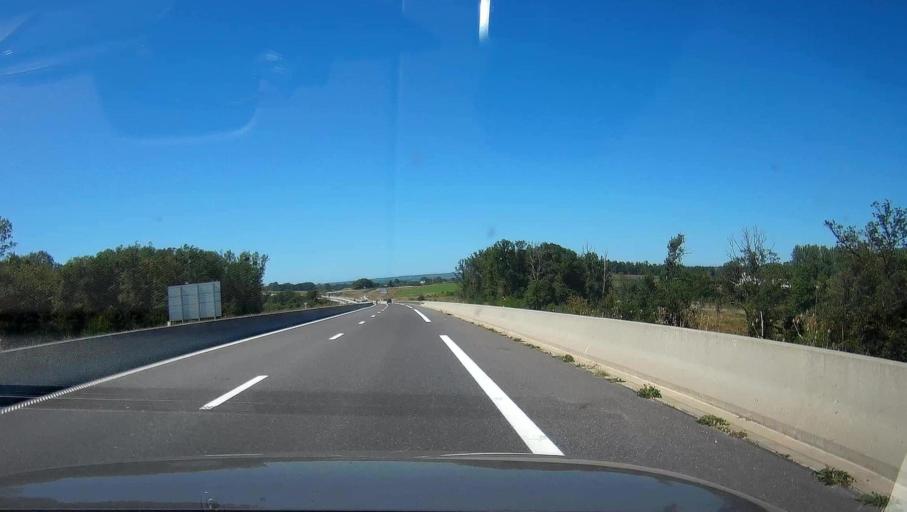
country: FR
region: Champagne-Ardenne
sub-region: Departement des Ardennes
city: Warcq
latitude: 49.7596
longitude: 4.6518
